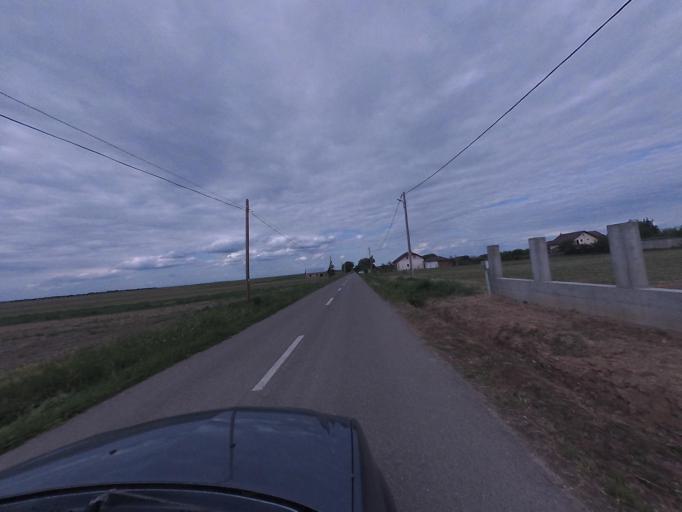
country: RO
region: Neamt
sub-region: Comuna Trifesti
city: Miron Costin
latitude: 46.9559
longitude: 26.8112
